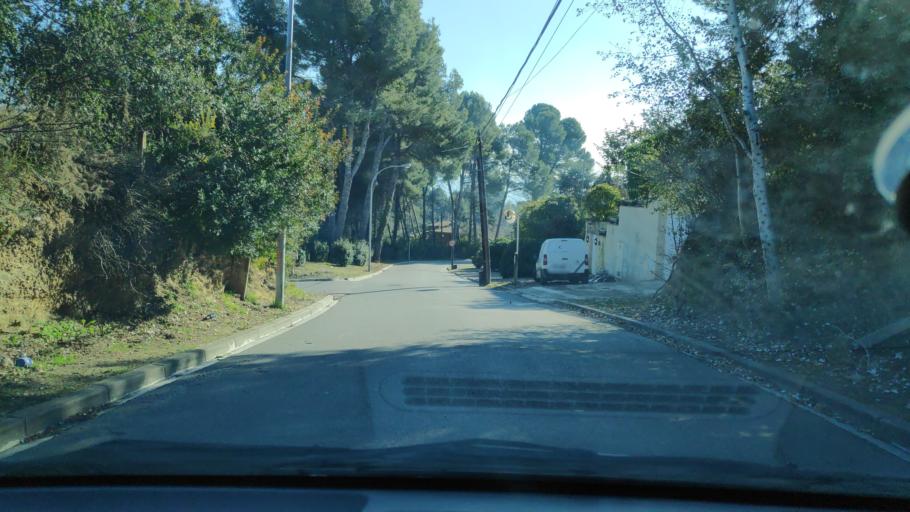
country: ES
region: Catalonia
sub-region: Provincia de Barcelona
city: Sant Cugat del Valles
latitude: 41.4971
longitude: 2.0816
